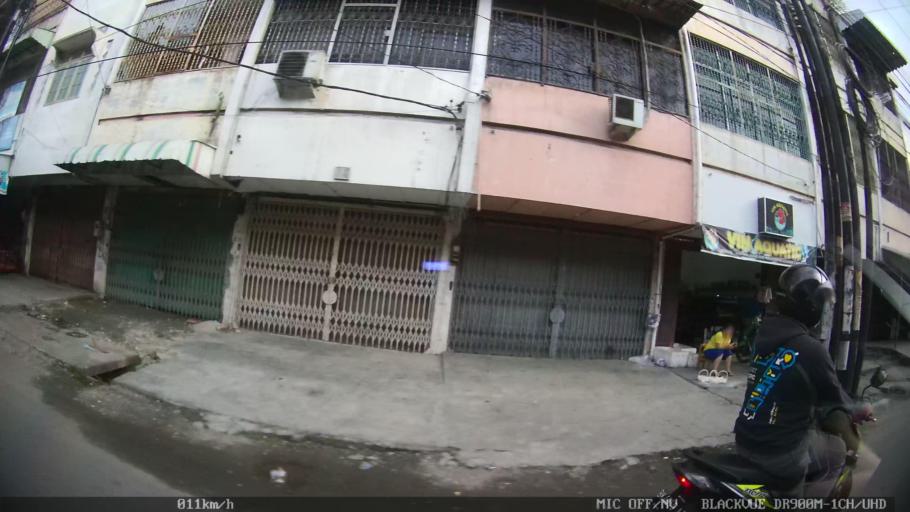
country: ID
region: North Sumatra
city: Medan
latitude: 3.5819
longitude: 98.7019
